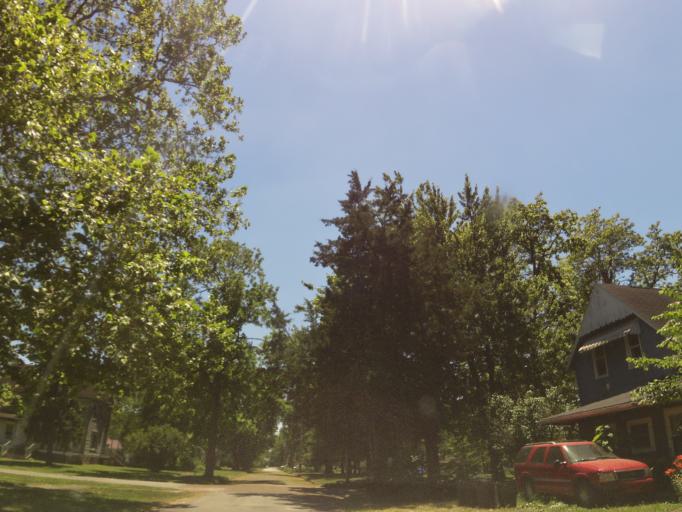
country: US
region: Illinois
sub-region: Livingston County
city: Chatsworth
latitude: 40.7566
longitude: -88.1850
